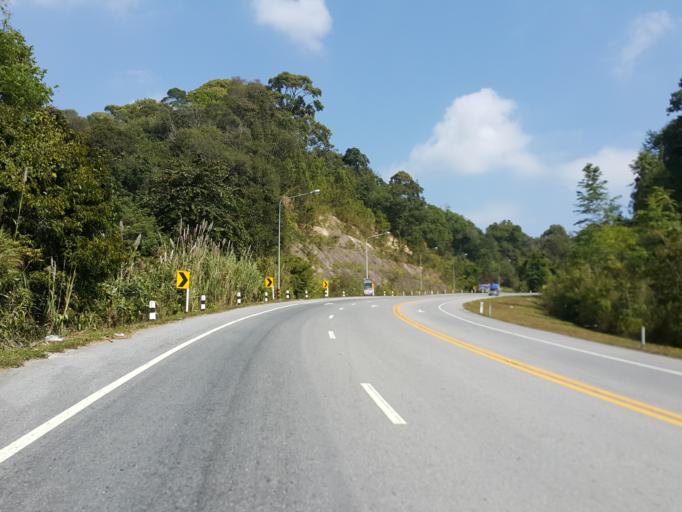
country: TH
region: Lampang
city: Wang Nuea
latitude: 19.0661
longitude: 99.3751
